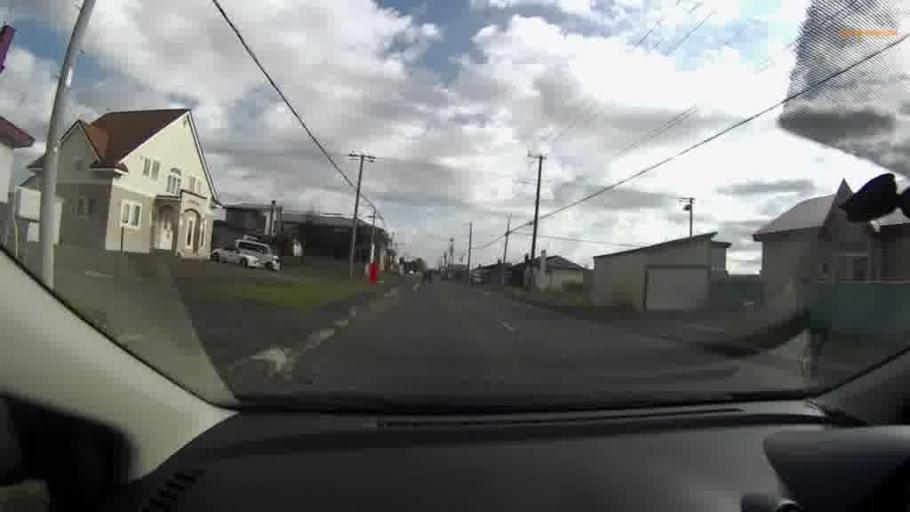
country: JP
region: Hokkaido
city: Kushiro
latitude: 42.9775
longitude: 144.1266
